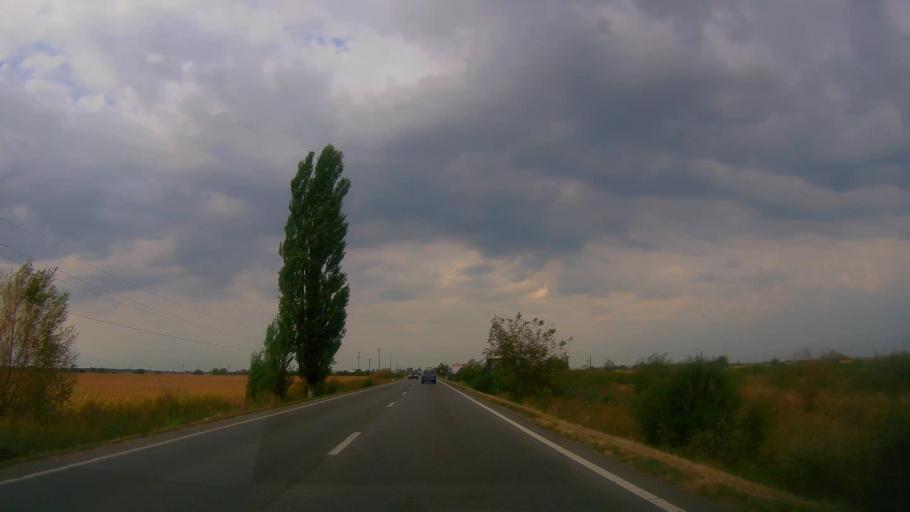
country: RO
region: Satu Mare
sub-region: Comuna Botiz
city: Botiz
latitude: 47.8139
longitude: 22.9263
